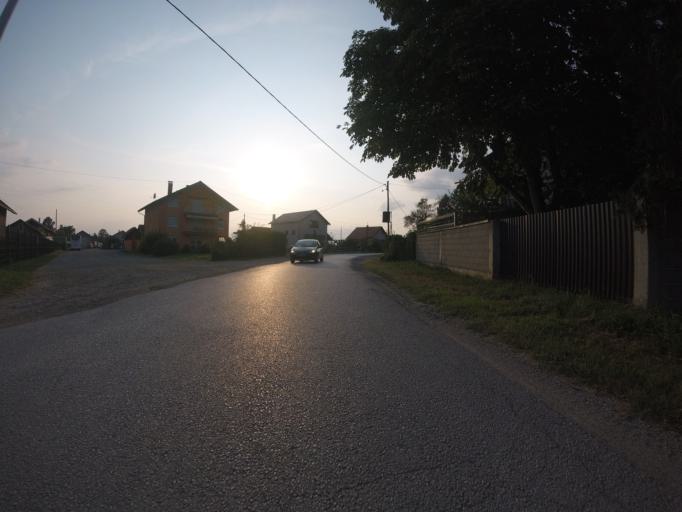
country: HR
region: Zagrebacka
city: Micevec
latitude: 45.7509
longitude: 16.1327
